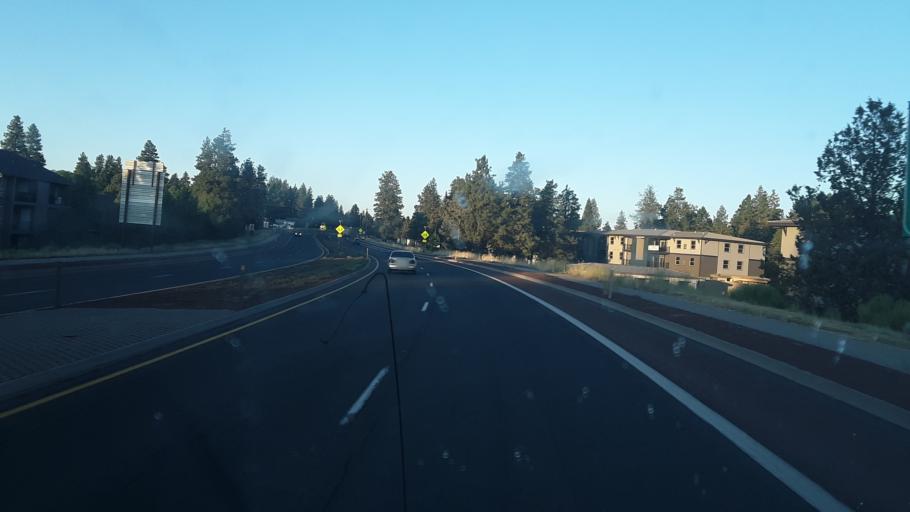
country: US
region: Oregon
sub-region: Deschutes County
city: Bend
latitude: 44.0351
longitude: -121.3130
